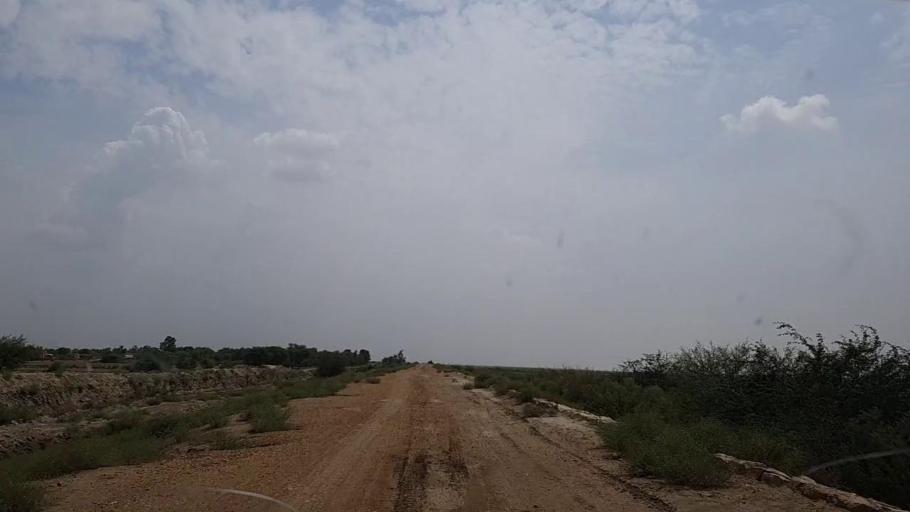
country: PK
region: Sindh
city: Phulji
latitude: 26.8105
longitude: 67.6070
